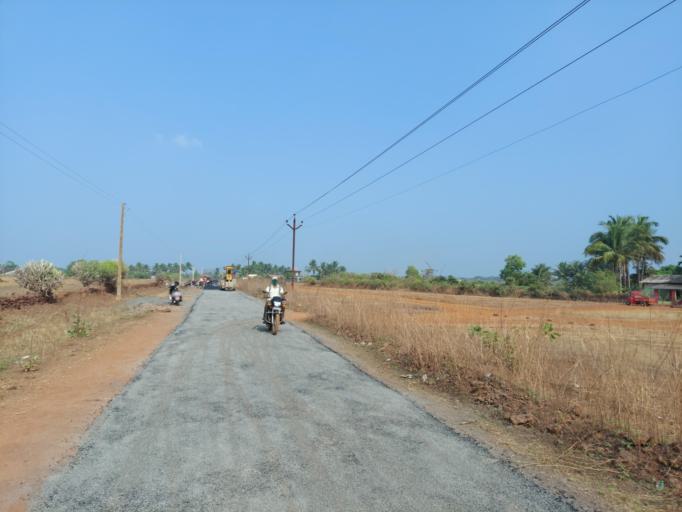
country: IN
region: Maharashtra
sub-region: Ratnagiri
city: Ratnagiri
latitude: 16.9249
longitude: 73.3176
